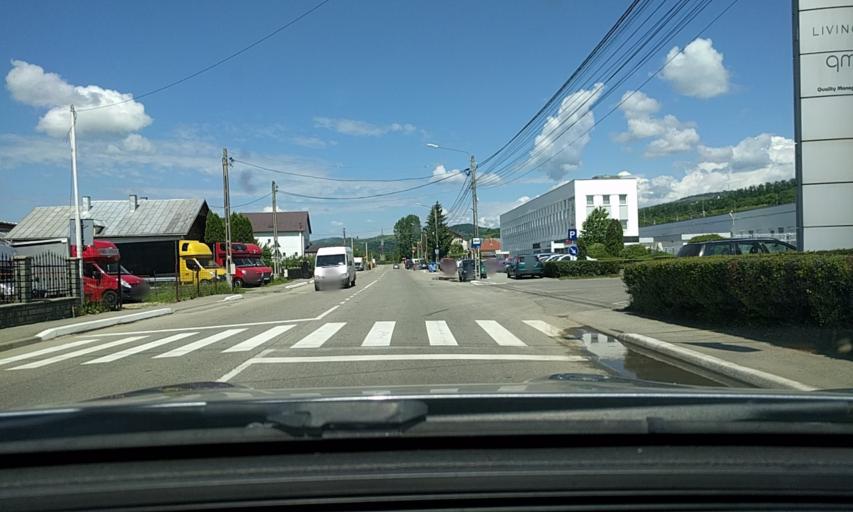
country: RO
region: Bistrita-Nasaud
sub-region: Oras Nasaud
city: Nasaud
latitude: 47.2952
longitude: 24.3829
